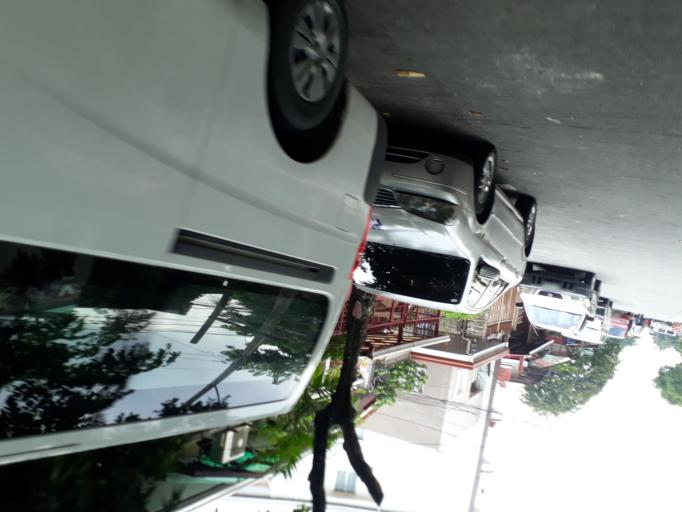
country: PH
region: Calabarzon
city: Bagong Pagasa
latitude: 14.6635
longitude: 121.0318
